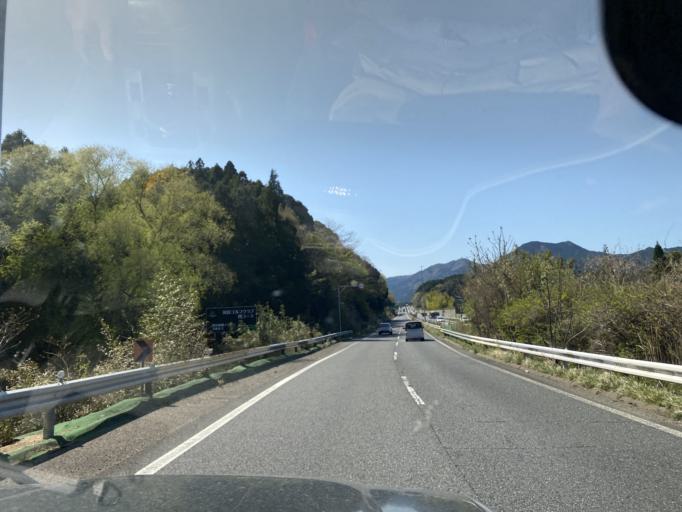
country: JP
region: Mie
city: Kameyama
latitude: 34.8361
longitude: 136.3363
